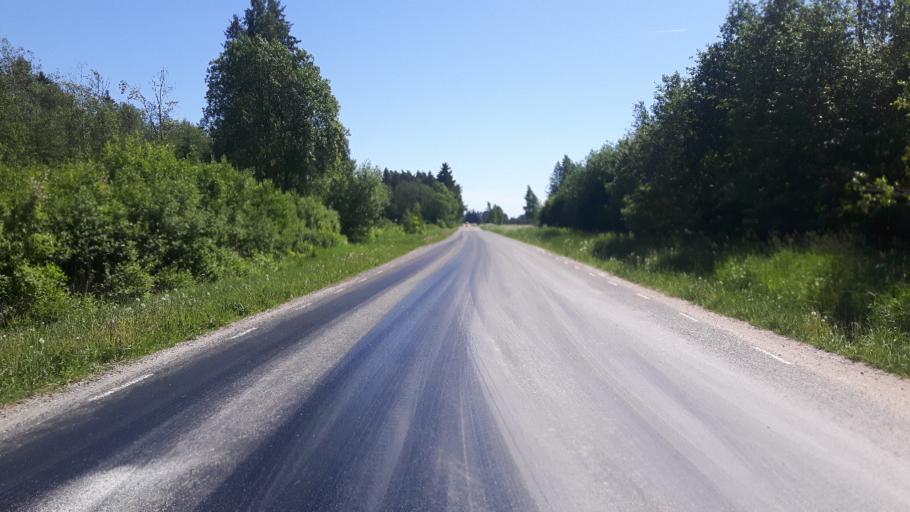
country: EE
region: Raplamaa
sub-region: Kohila vald
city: Kohila
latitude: 59.2028
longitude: 24.6896
